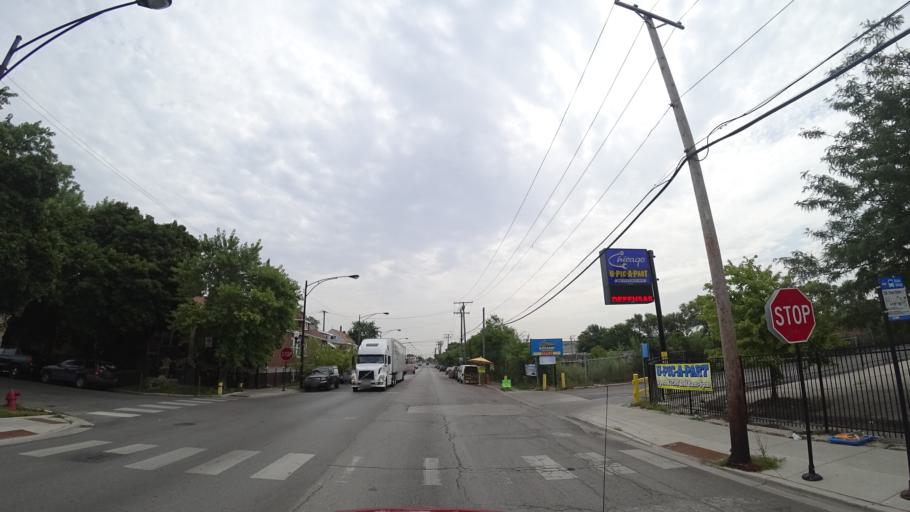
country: US
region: Illinois
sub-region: Cook County
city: Cicero
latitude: 41.8371
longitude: -87.7124
